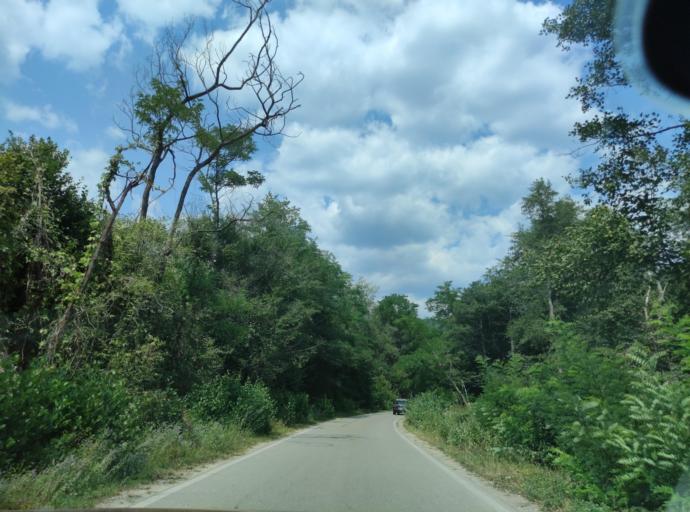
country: BG
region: Blagoevgrad
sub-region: Obshtina Belitsa
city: Belitsa
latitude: 41.9956
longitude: 23.5496
